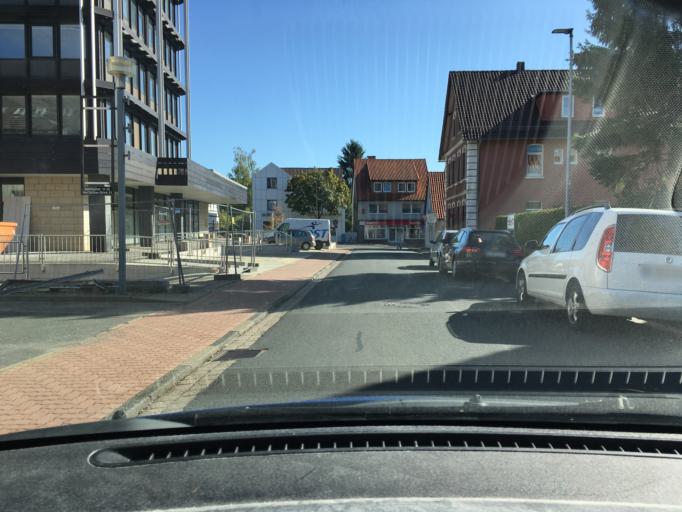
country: DE
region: Lower Saxony
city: Springe
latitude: 52.2111
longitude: 9.5569
